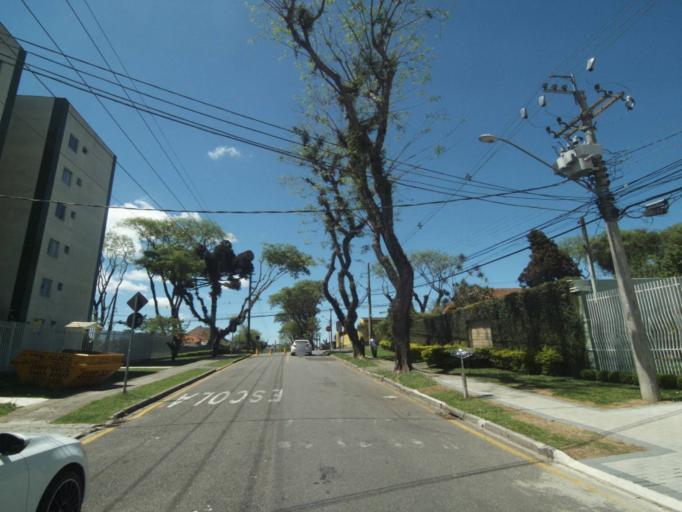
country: BR
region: Parana
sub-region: Curitiba
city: Curitiba
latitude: -25.3914
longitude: -49.2428
